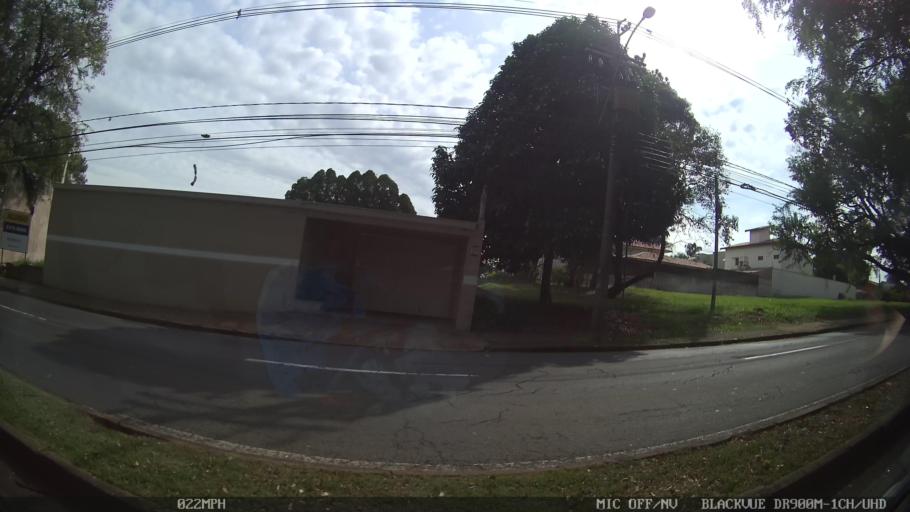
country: BR
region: Sao Paulo
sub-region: Piracicaba
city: Piracicaba
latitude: -22.7228
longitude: -47.6650
